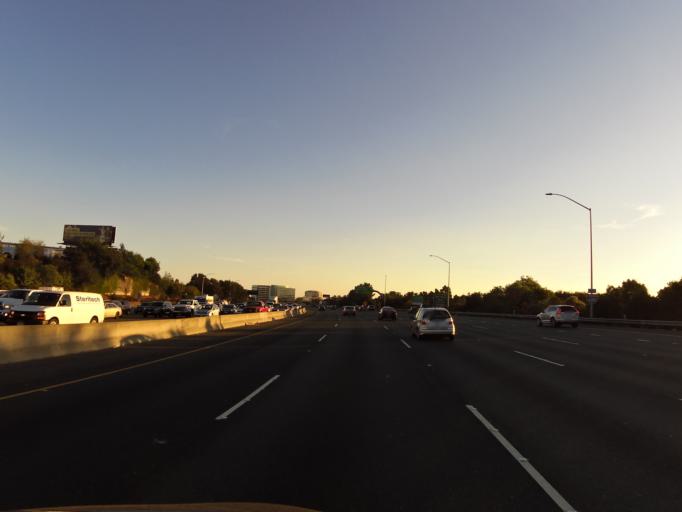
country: US
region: California
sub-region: Contra Costa County
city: Walnut Creek
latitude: 37.9178
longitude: -122.0636
